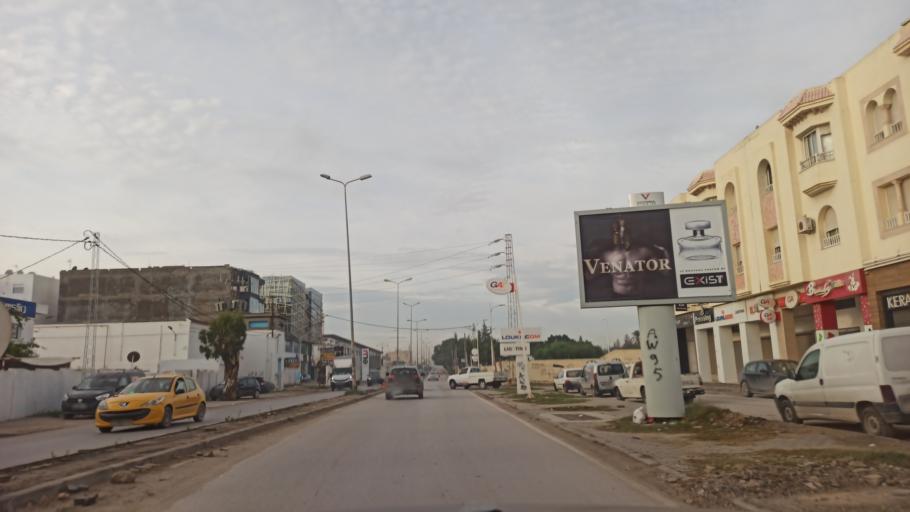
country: TN
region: Ariana
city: Ariana
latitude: 36.8690
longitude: 10.2273
